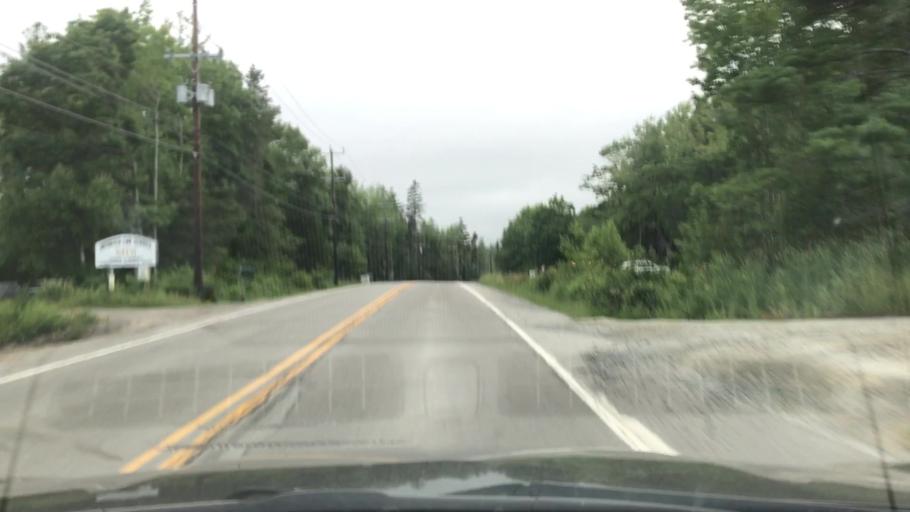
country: US
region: Maine
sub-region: Hancock County
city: Trenton
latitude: 44.4081
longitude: -68.3506
